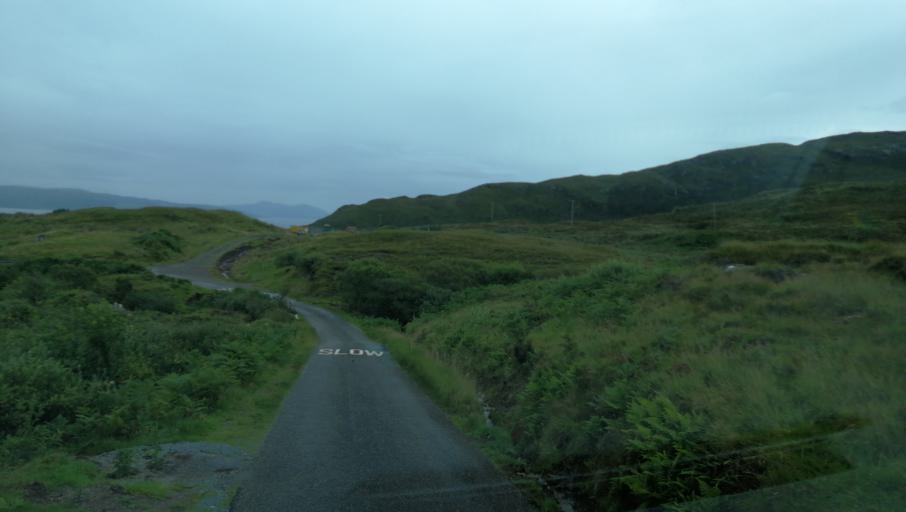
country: GB
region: Scotland
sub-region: Argyll and Bute
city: Isle Of Mull
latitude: 56.7096
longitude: -6.1388
